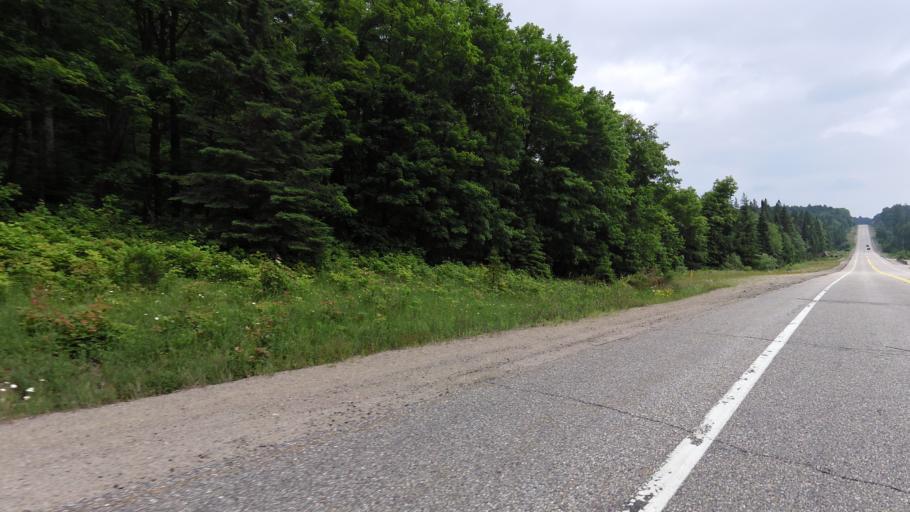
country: CA
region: Ontario
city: Huntsville
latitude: 45.5595
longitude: -78.5797
